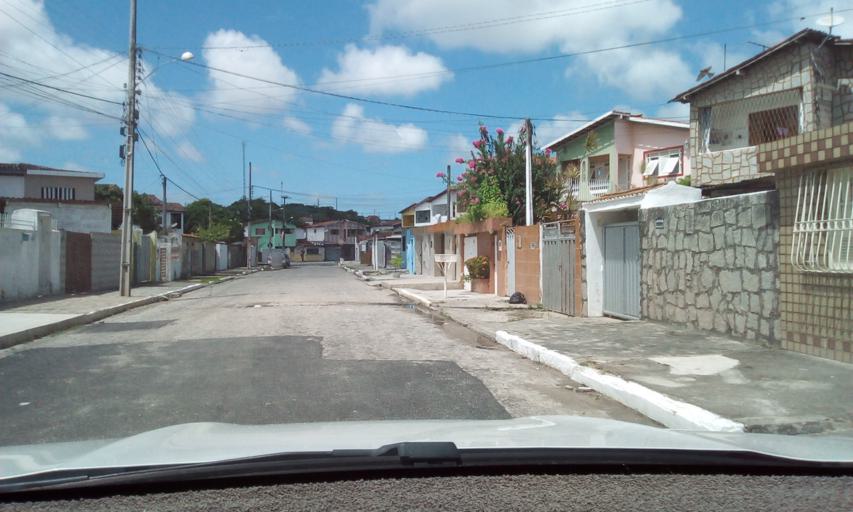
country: BR
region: Paraiba
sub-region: Joao Pessoa
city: Joao Pessoa
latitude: -7.1690
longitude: -34.8888
